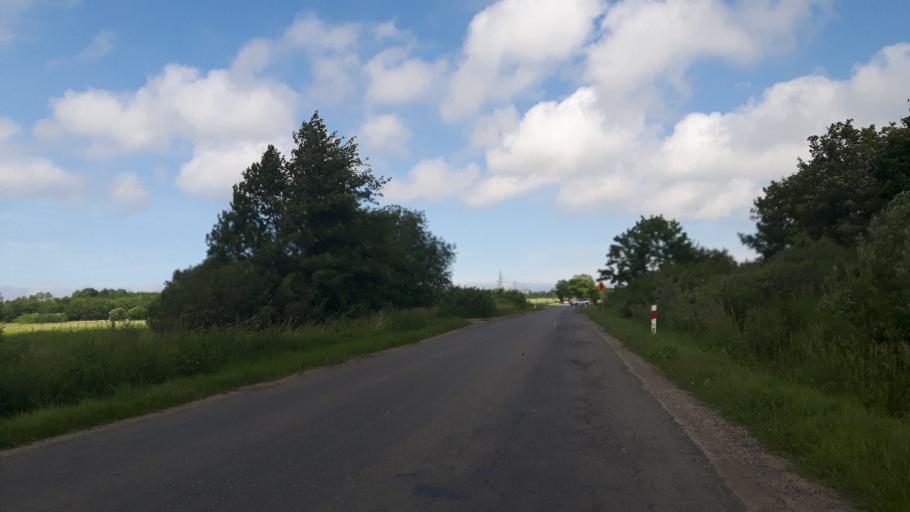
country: PL
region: Pomeranian Voivodeship
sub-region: Powiat slupski
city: Ustka
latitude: 54.5516
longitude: 16.8355
